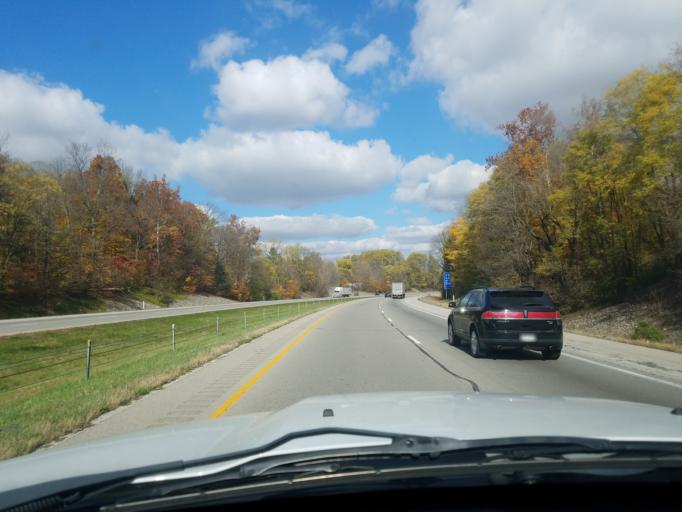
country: US
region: Indiana
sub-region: Bartholomew County
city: Lowell
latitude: 39.2968
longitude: -85.9673
